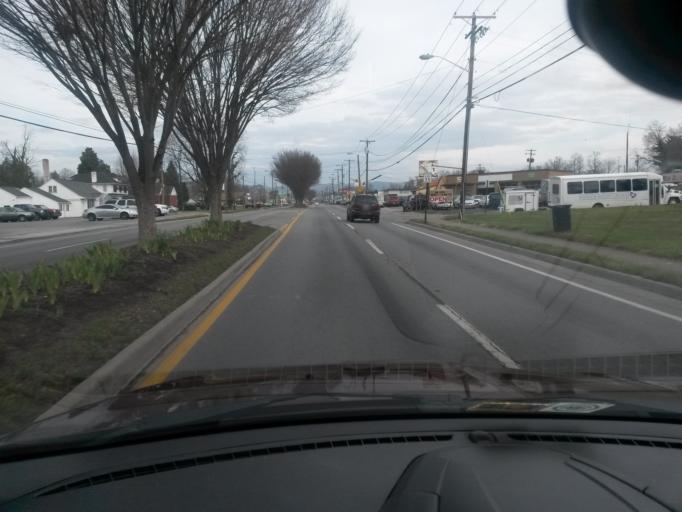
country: US
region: Virginia
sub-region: Roanoke County
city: Hollins
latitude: 37.3087
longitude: -79.9485
